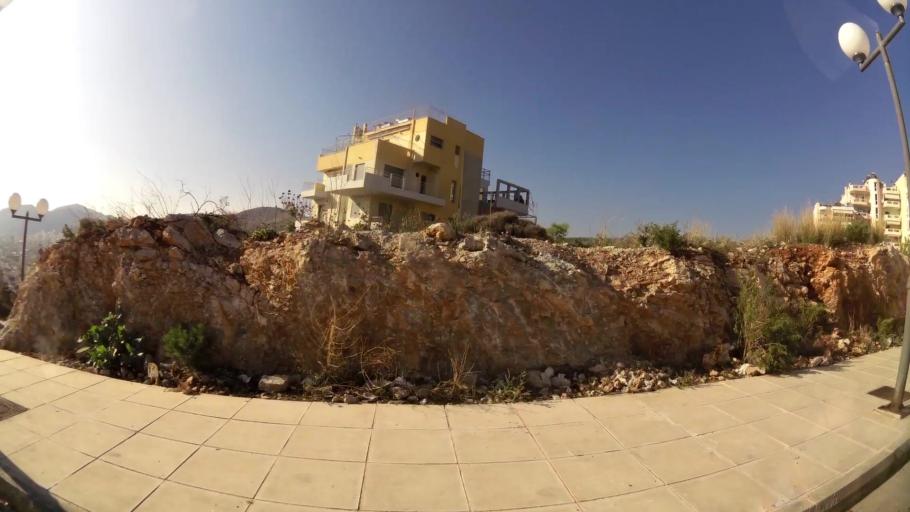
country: GR
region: Attica
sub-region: Nomos Piraios
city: Keratsini
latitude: 37.9711
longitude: 23.6300
